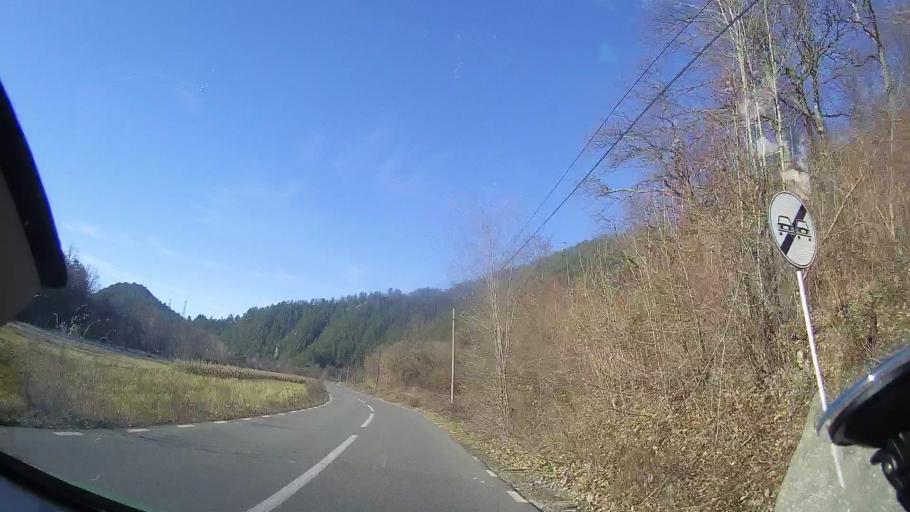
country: RO
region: Bihor
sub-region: Comuna Bratca
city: Bratca
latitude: 46.9297
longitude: 22.6405
